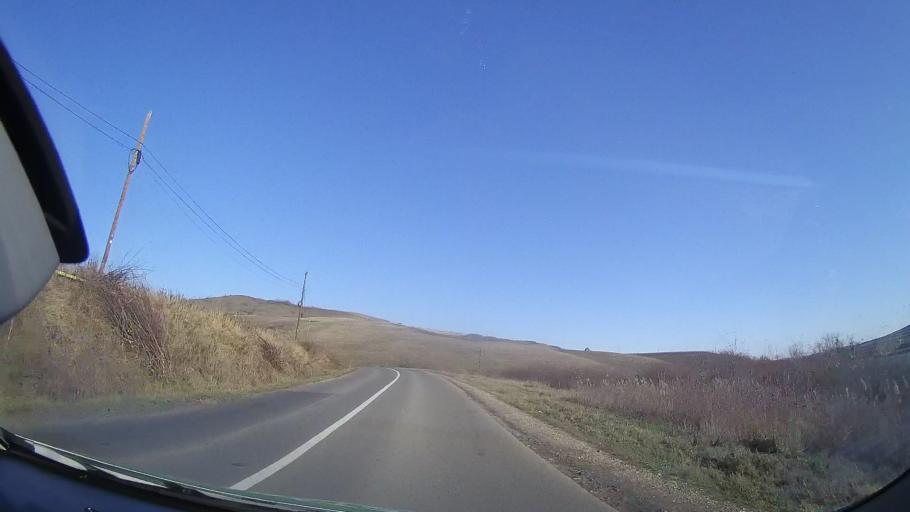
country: RO
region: Mures
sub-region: Comuna Mihesu de Campie
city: Mihesu de Campie
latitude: 46.6563
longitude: 24.1750
